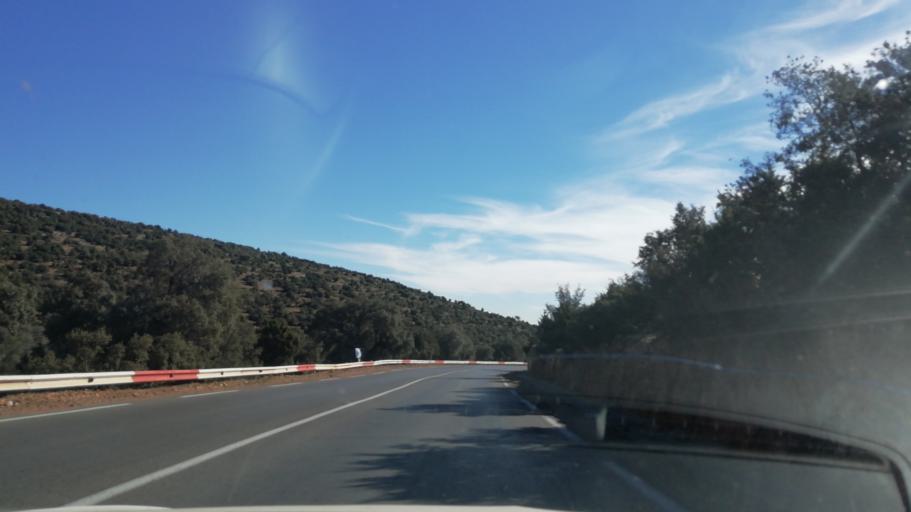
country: DZ
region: Tlemcen
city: Sebdou
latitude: 34.7389
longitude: -1.3384
